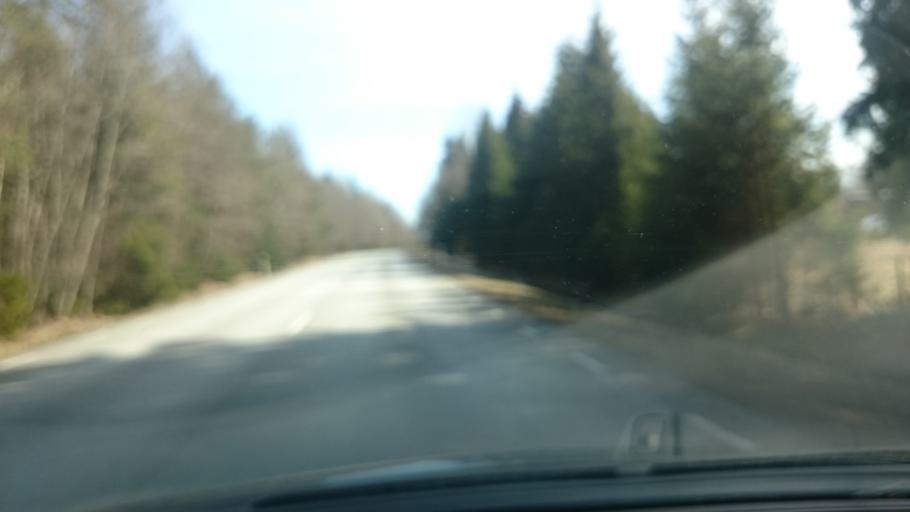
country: EE
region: Paernumaa
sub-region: Tootsi vald
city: Tootsi
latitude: 58.6632
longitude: 24.8148
